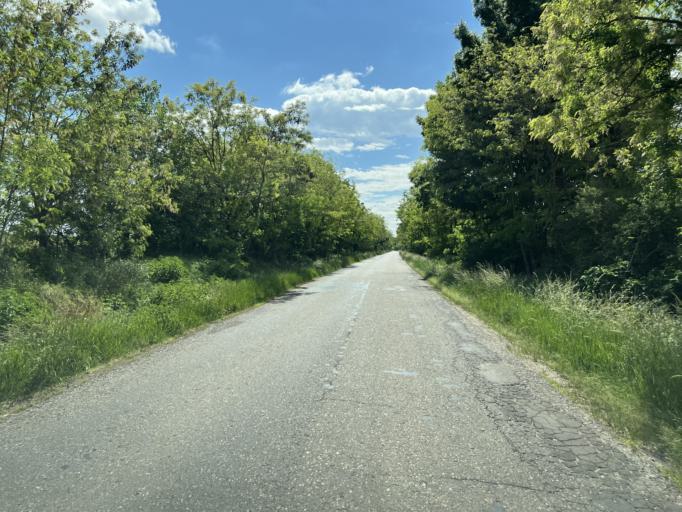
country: HU
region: Pest
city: Vacszentlaszlo
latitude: 47.5642
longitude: 19.5527
